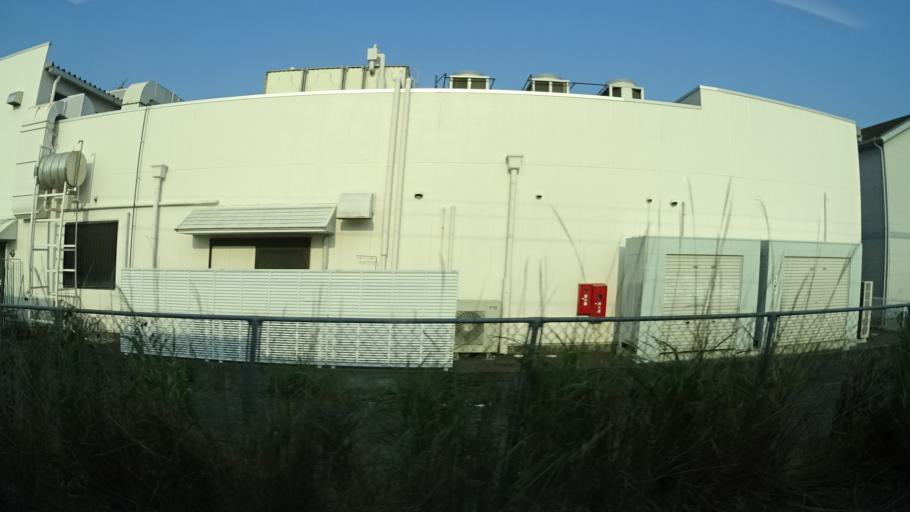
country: JP
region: Ibaraki
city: Hitachi
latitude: 36.5390
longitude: 140.6238
